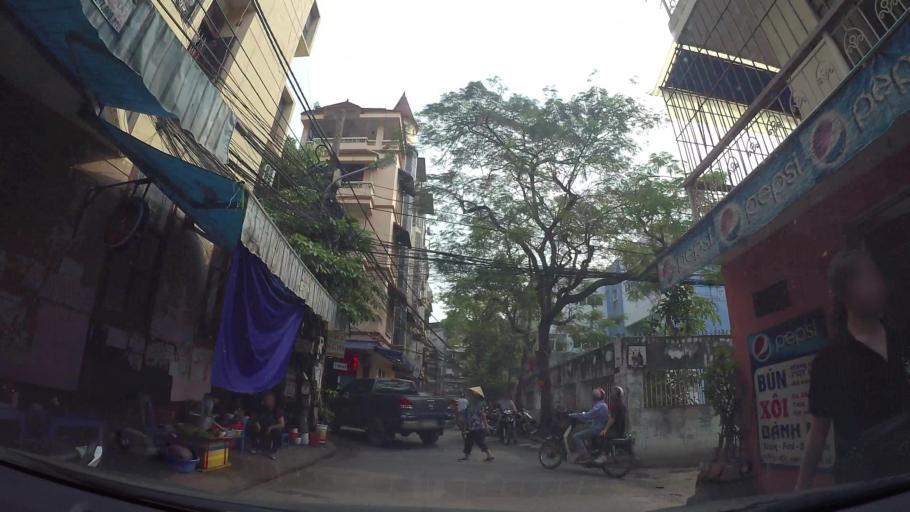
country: VN
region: Ha Noi
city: Cau Giay
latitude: 21.0195
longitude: 105.8110
